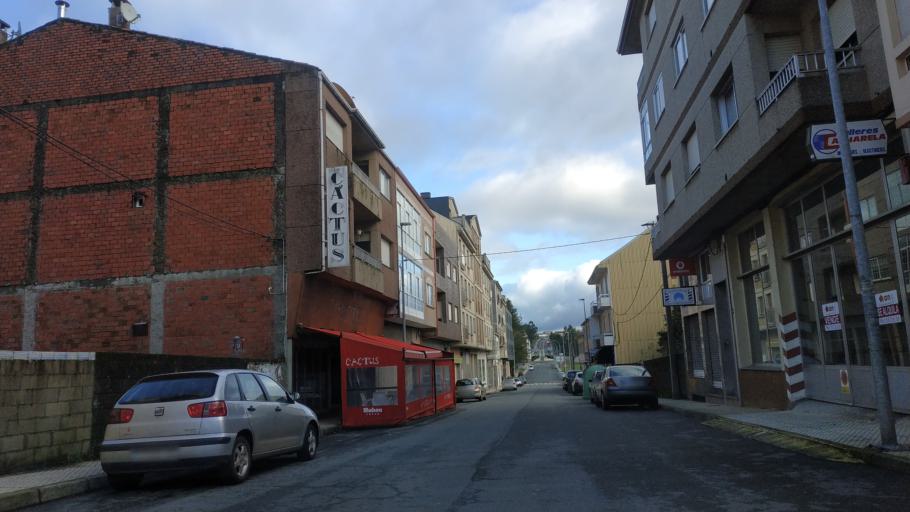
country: ES
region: Galicia
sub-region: Provincia de Pontevedra
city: Silleda
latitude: 42.7931
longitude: -8.1659
